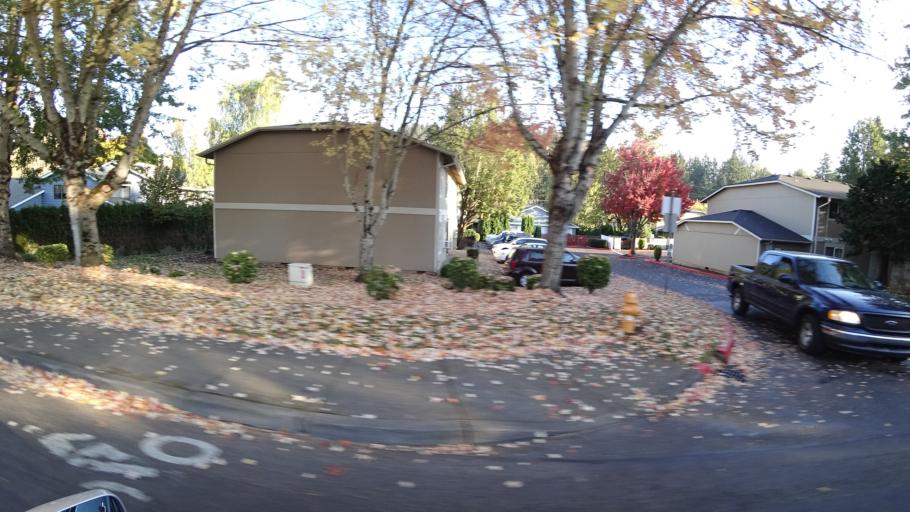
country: US
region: Oregon
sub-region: Multnomah County
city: Gresham
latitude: 45.4925
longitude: -122.4461
